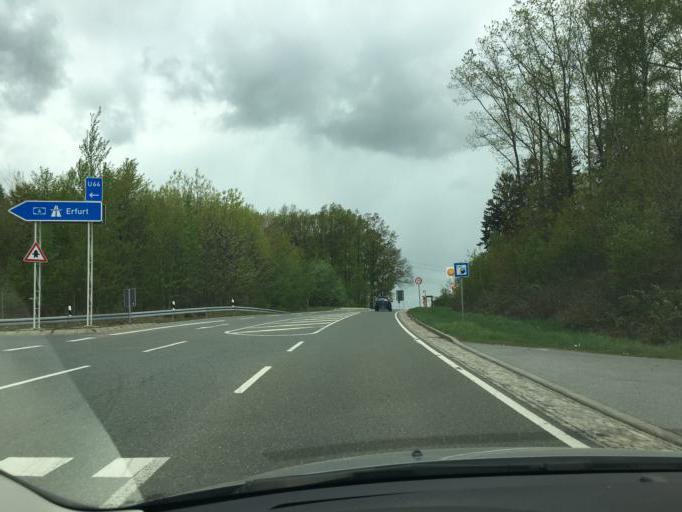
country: DE
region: Saxony
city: Limbach-Oberfrohna
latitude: 50.8214
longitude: 12.7550
